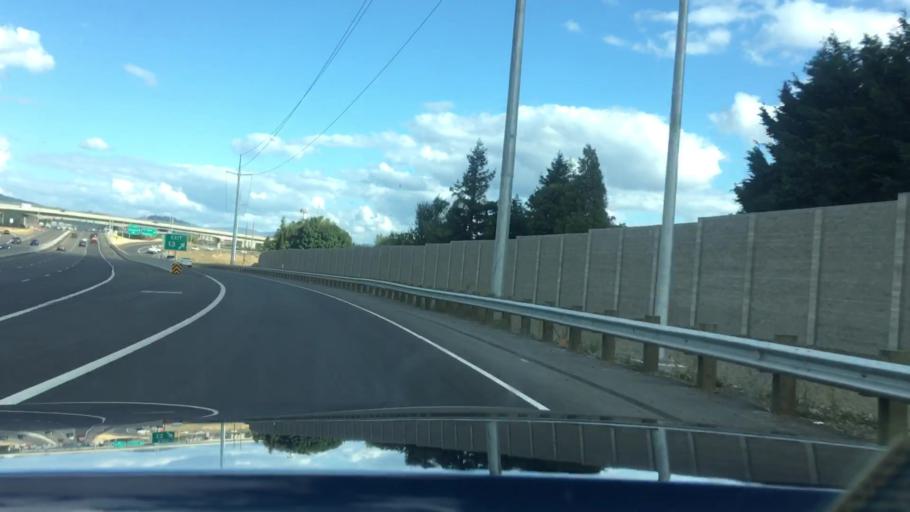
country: US
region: Oregon
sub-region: Lane County
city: Eugene
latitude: 44.0838
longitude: -123.0556
